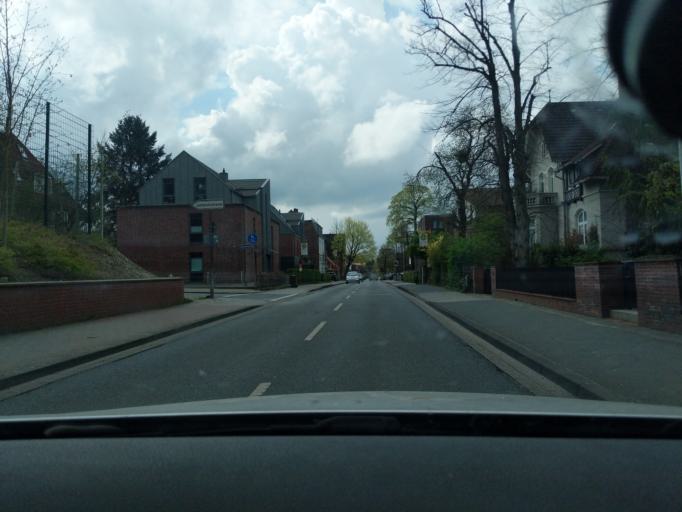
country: DE
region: Lower Saxony
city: Stade
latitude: 53.5906
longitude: 9.4688
